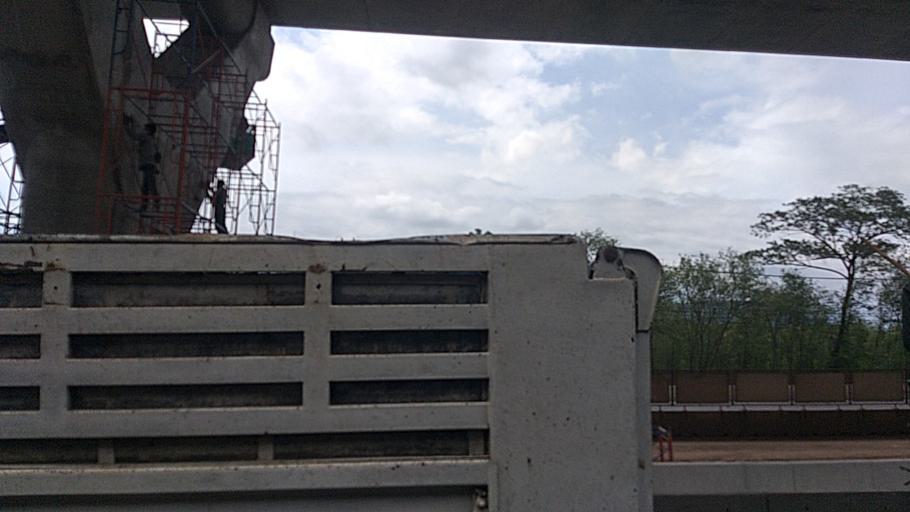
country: TH
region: Nakhon Ratchasima
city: Amphoe Sikhiu
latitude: 14.8484
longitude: 101.5658
